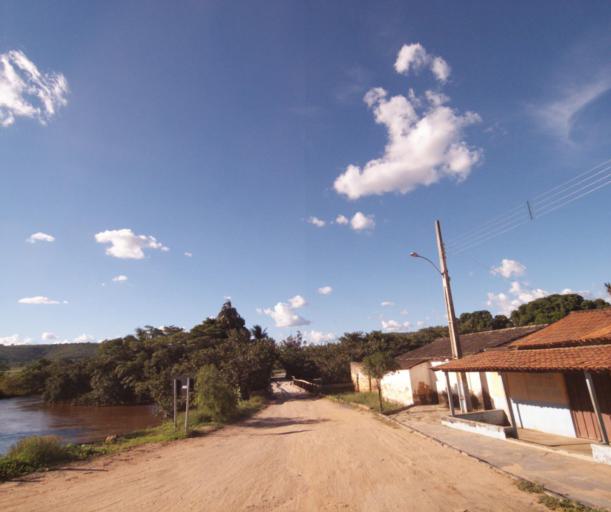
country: BR
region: Minas Gerais
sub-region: Manga
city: Manga
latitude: -14.3136
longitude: -44.4609
